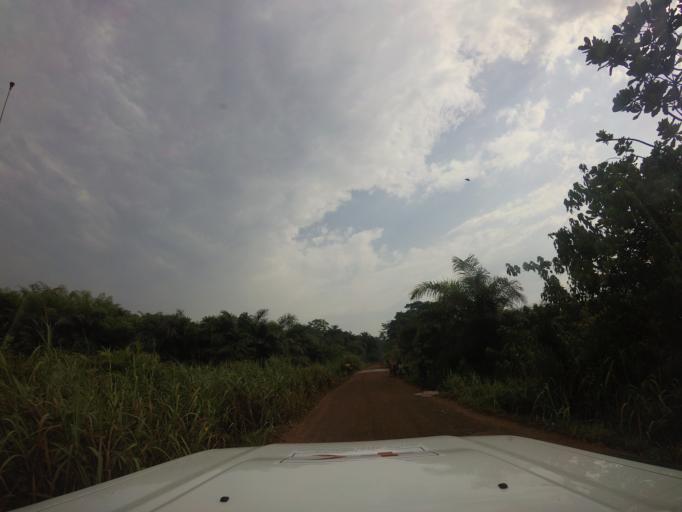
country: LR
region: Grand Cape Mount
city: Robertsport
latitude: 7.0170
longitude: -11.2880
